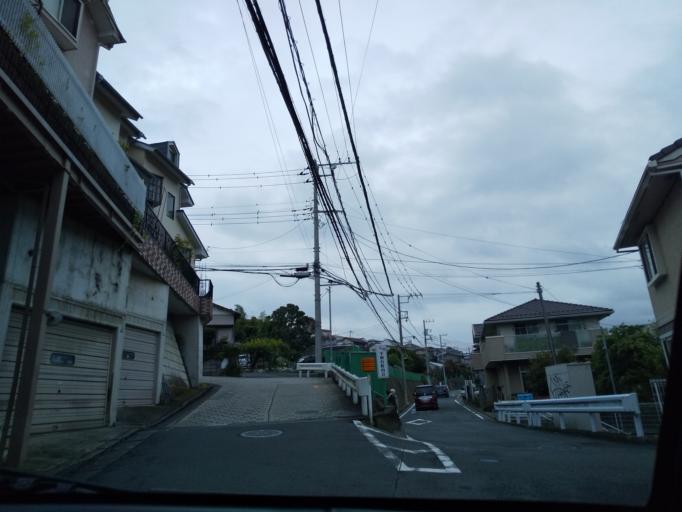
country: JP
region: Kanagawa
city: Fujisawa
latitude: 35.3932
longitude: 139.5151
